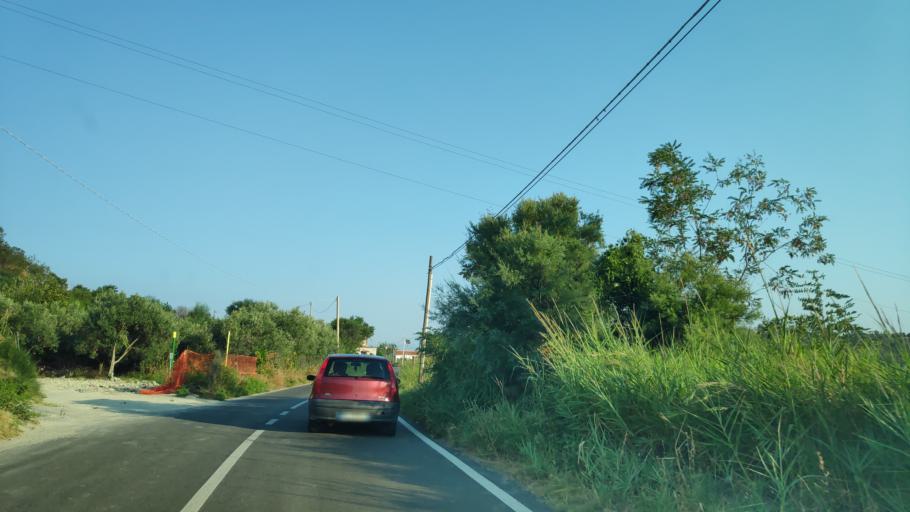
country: IT
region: Calabria
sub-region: Provincia di Reggio Calabria
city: Caulonia Marina
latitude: 38.3707
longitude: 16.4463
